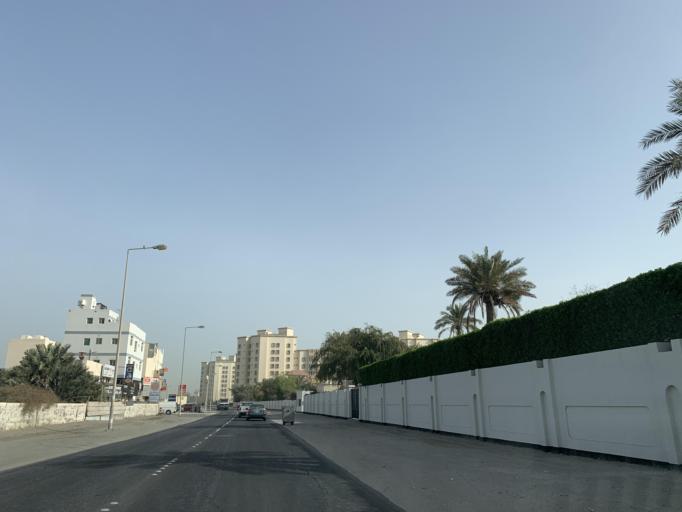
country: BH
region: Northern
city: Madinat `Isa
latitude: 26.1818
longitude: 50.5599
